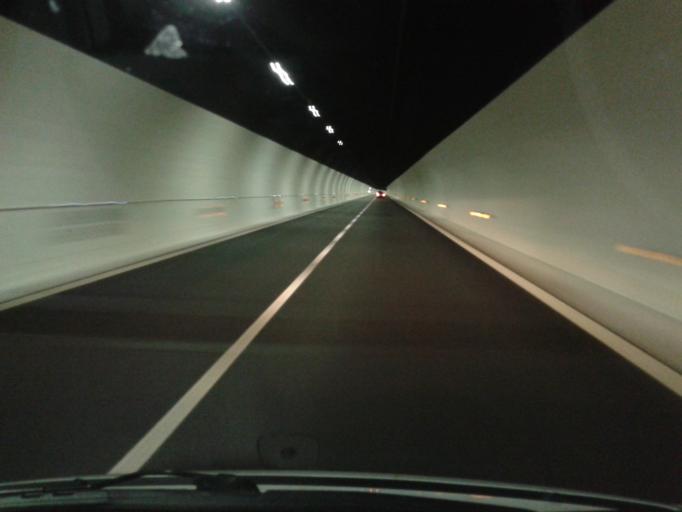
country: IT
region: Friuli Venezia Giulia
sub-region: Provincia di Udine
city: Chiusaforte
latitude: 46.3990
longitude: 13.2742
